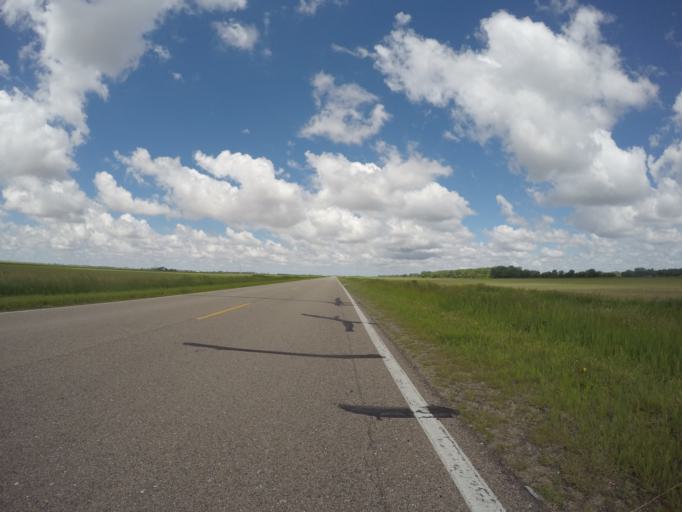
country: US
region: Nebraska
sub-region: Buffalo County
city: Kearney
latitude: 40.6570
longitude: -99.2410
